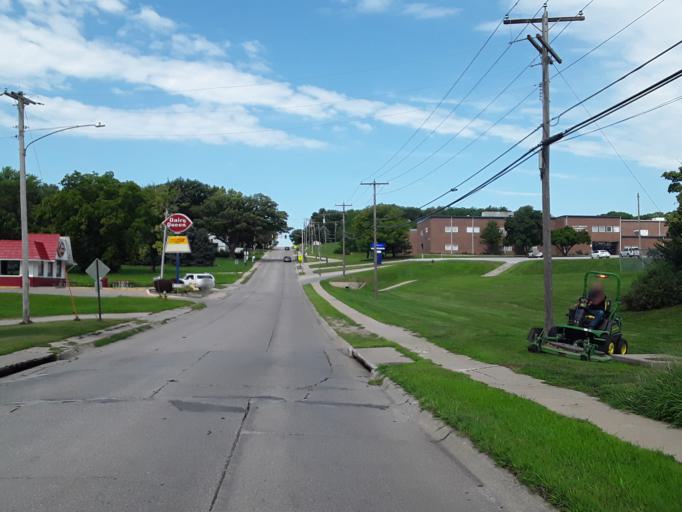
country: US
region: Nebraska
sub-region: Cass County
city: Plattsmouth
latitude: 41.0025
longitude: -95.8980
